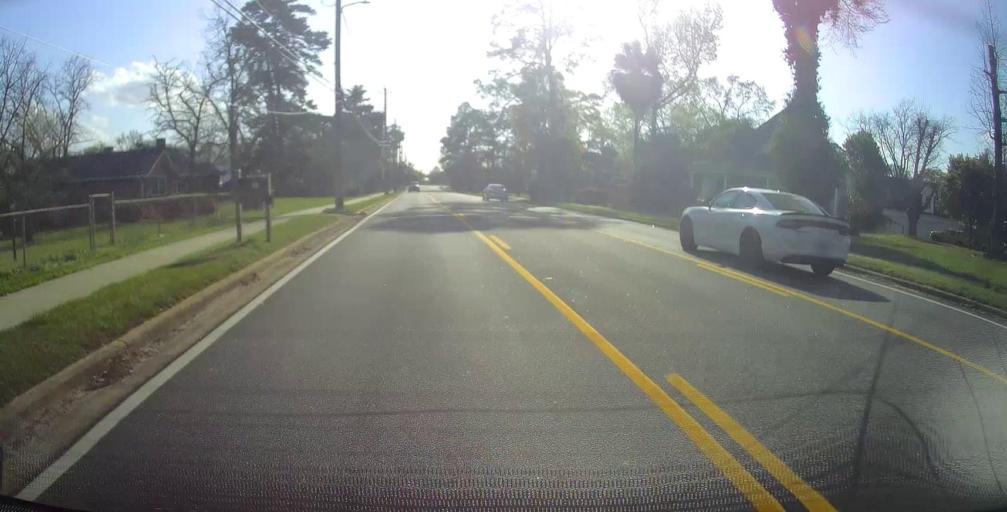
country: US
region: Georgia
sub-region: Montgomery County
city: Mount Vernon
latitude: 32.1802
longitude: -82.5898
